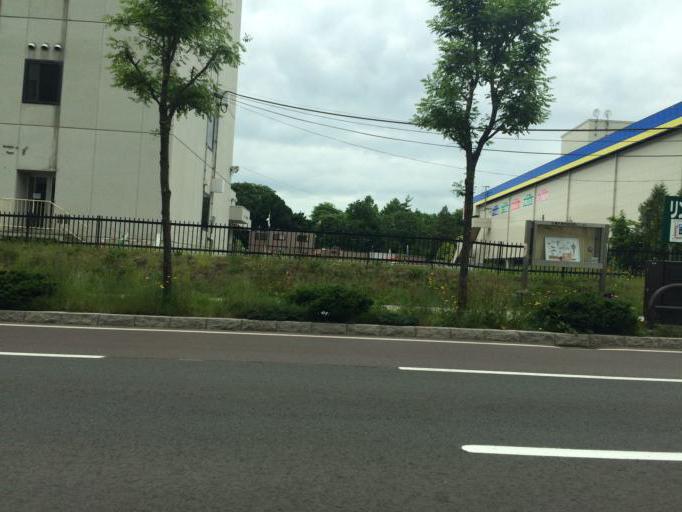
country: JP
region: Hokkaido
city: Sapporo
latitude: 43.0609
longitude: 141.3435
